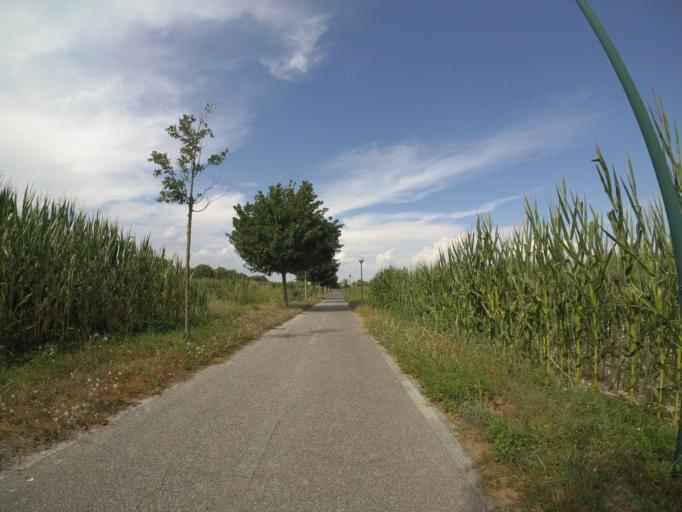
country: IT
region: Friuli Venezia Giulia
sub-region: Provincia di Udine
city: Lignano Sabbiadoro
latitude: 45.6692
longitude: 13.0706
